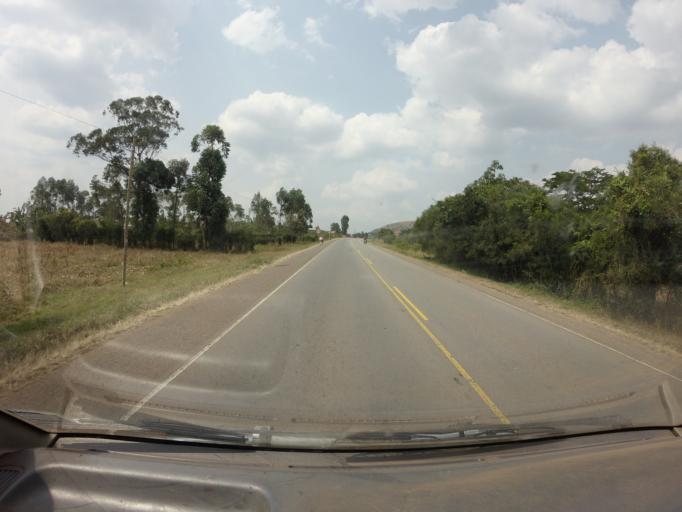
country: UG
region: Central Region
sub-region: Lyantonde District
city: Lyantonde
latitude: -0.3928
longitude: 31.1816
